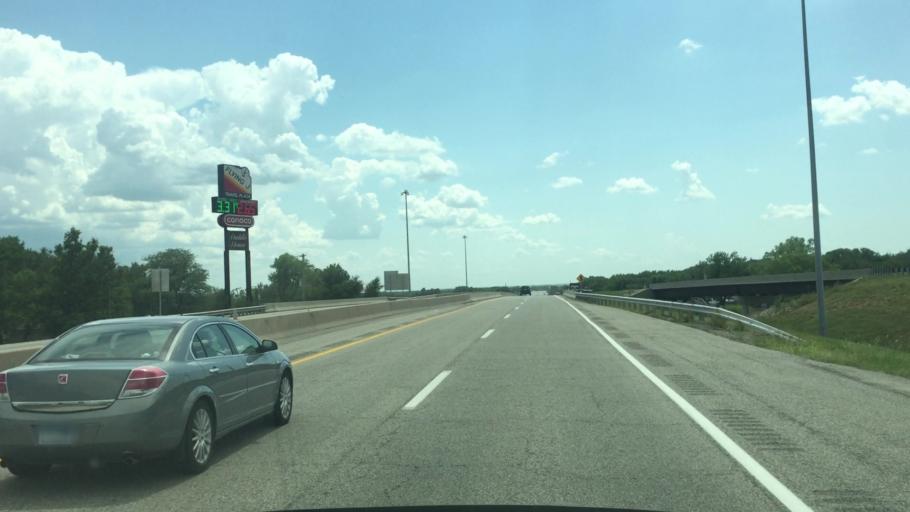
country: US
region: Kansas
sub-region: Lyon County
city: Emporia
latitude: 38.4132
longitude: -96.2390
